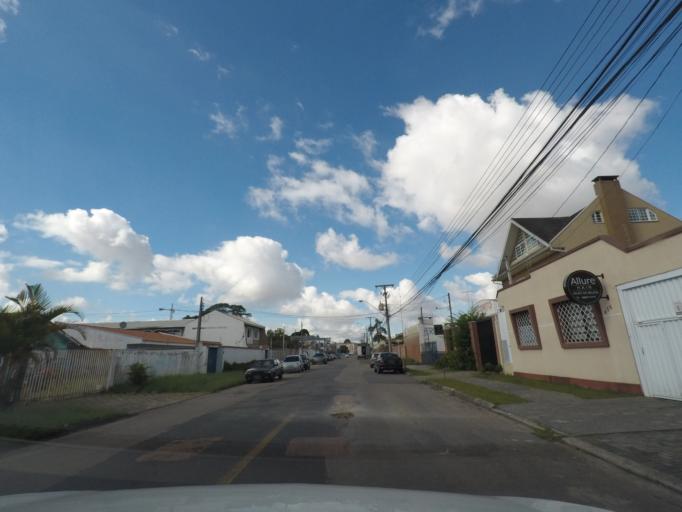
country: BR
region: Parana
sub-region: Curitiba
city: Curitiba
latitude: -25.4459
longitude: -49.2579
